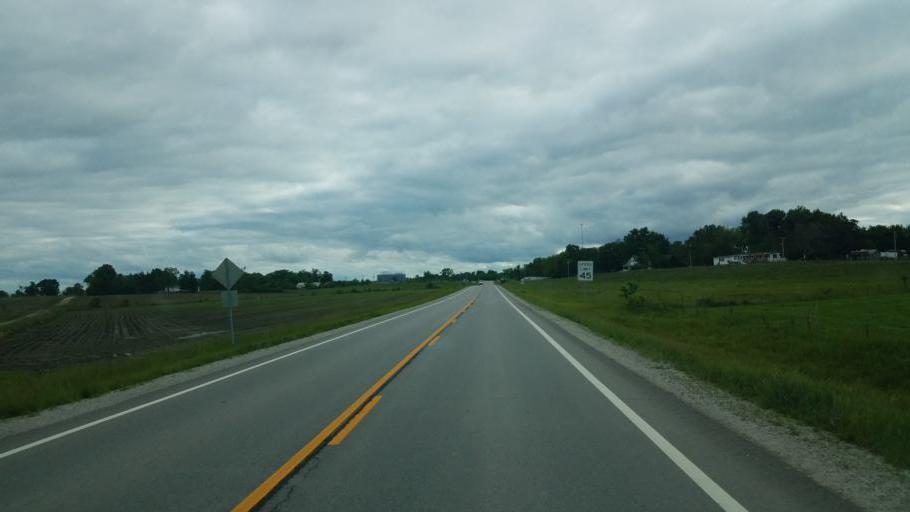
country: US
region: Missouri
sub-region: Mercer County
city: Princeton
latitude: 40.3294
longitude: -93.7948
